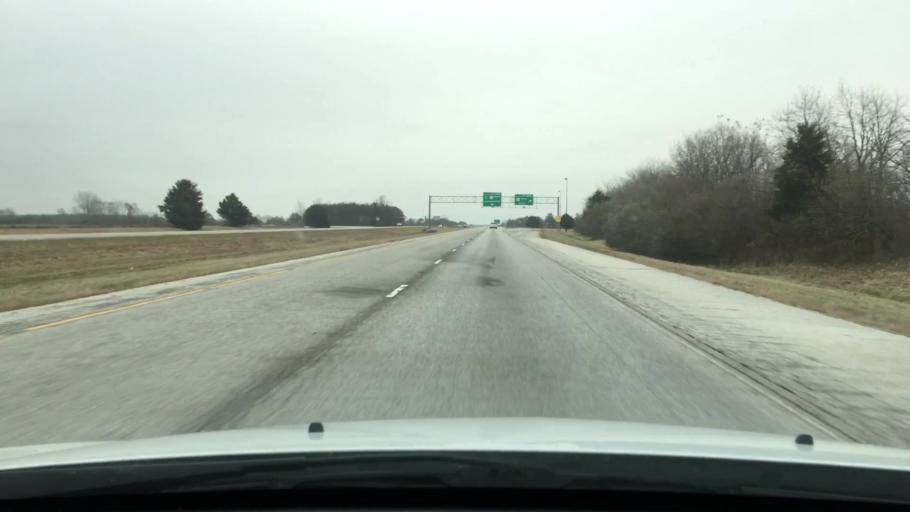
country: US
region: Illinois
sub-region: Morgan County
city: South Jacksonville
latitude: 39.6802
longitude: -90.3035
